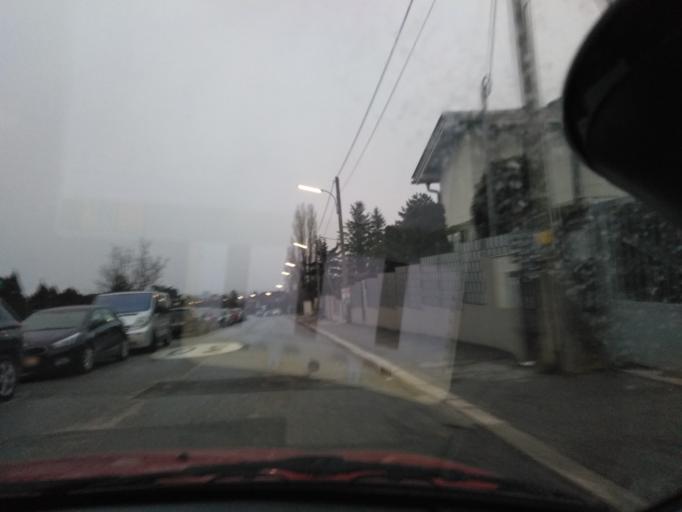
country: AT
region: Vienna
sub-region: Wien Stadt
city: Vienna
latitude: 48.2325
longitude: 16.3062
